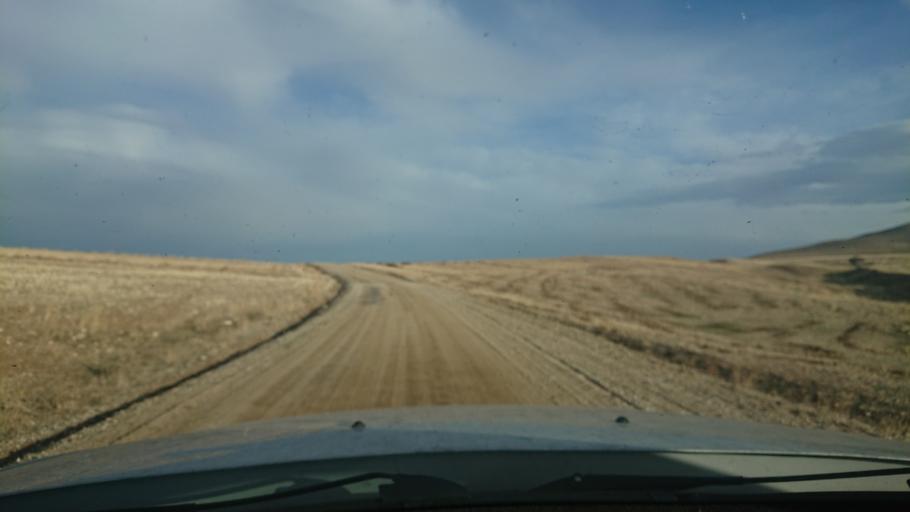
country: TR
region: Aksaray
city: Ortakoy
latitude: 38.7000
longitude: 33.8738
